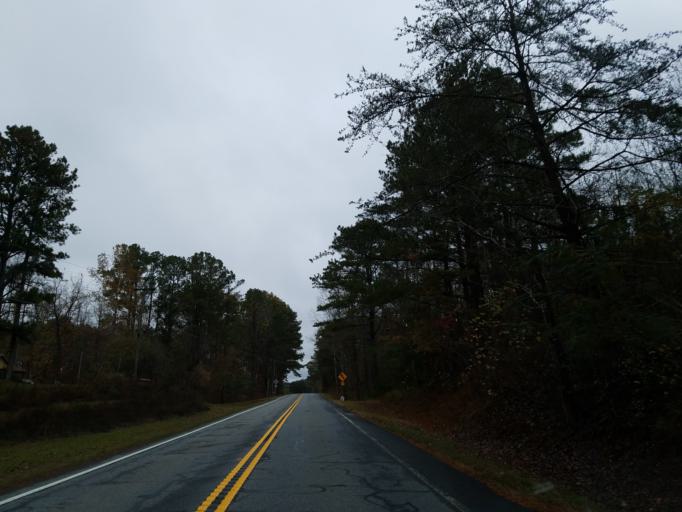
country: US
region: Georgia
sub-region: Cherokee County
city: Canton
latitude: 34.2707
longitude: -84.5835
